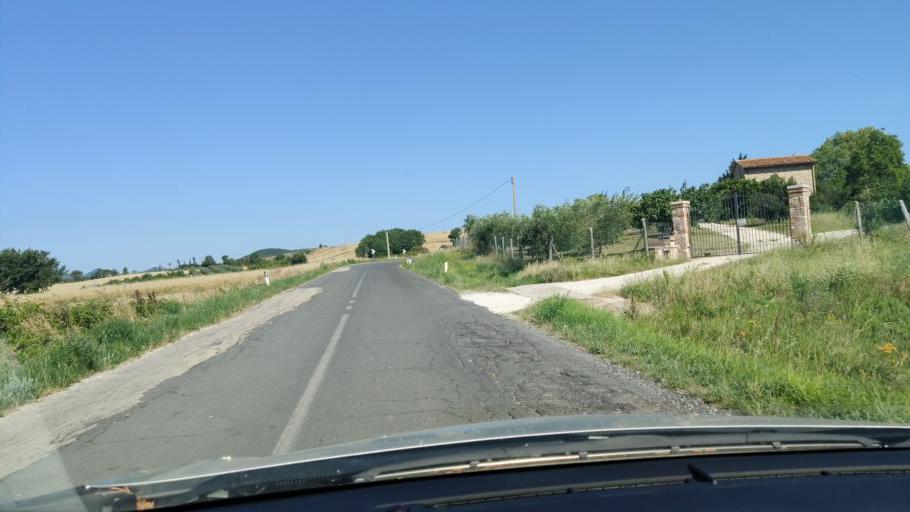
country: IT
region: Umbria
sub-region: Provincia di Terni
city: Avigliano Umbro
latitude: 42.6727
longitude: 12.4416
